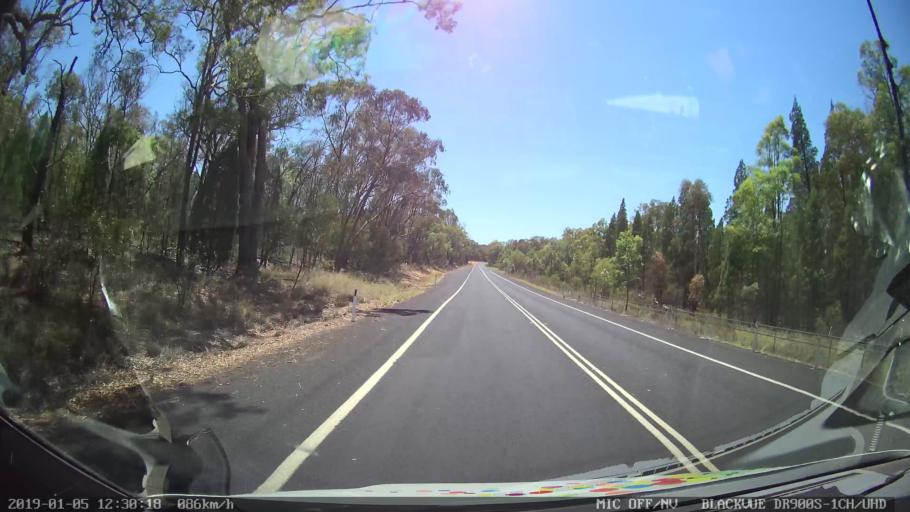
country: AU
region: New South Wales
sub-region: Warrumbungle Shire
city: Coonabarabran
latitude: -31.2289
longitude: 149.3488
